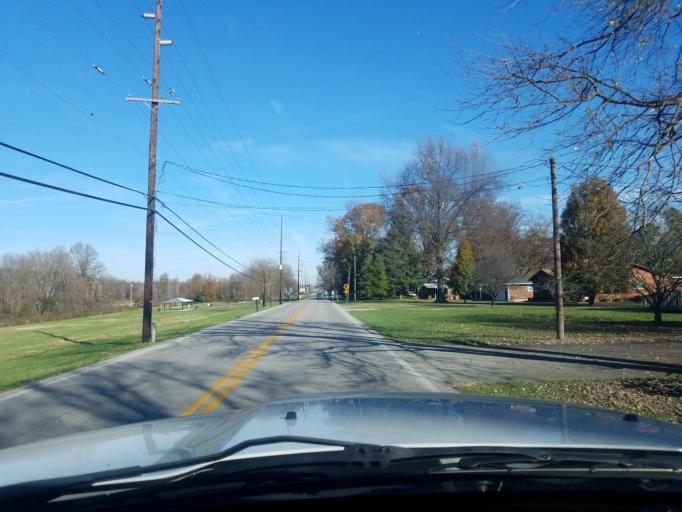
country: US
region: Kentucky
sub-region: Jefferson County
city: Pleasure Ridge Park
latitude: 38.1455
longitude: -85.8965
